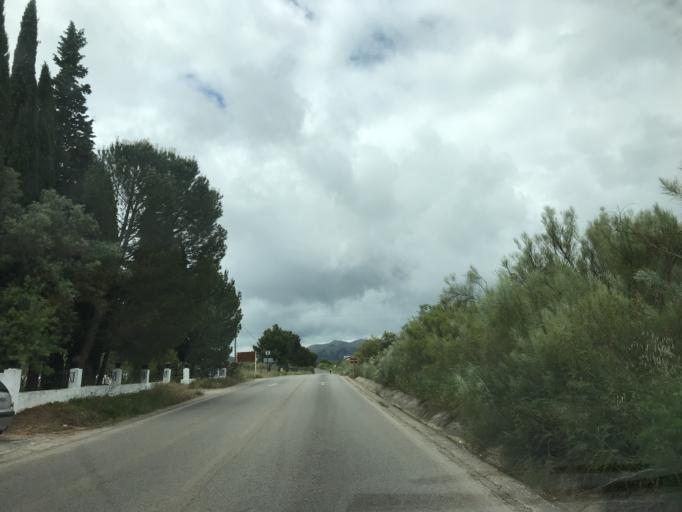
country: ES
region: Andalusia
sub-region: Provincia de Malaga
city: Ronda
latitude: 36.7278
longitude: -5.1695
